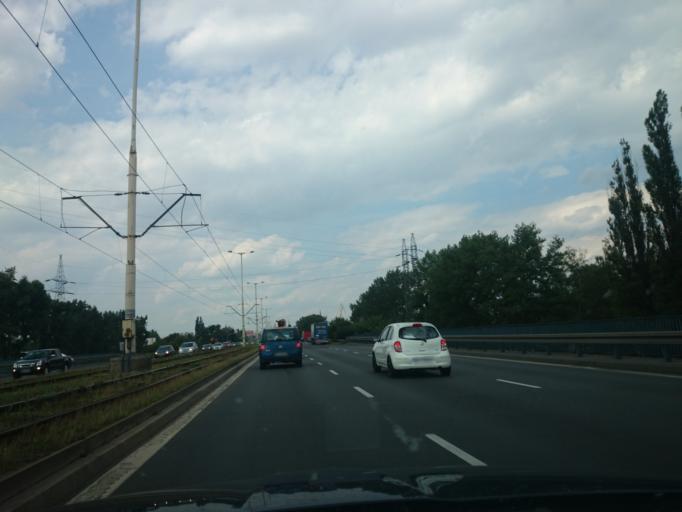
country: PL
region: West Pomeranian Voivodeship
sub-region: Szczecin
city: Szczecin
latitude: 53.4090
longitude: 14.5858
